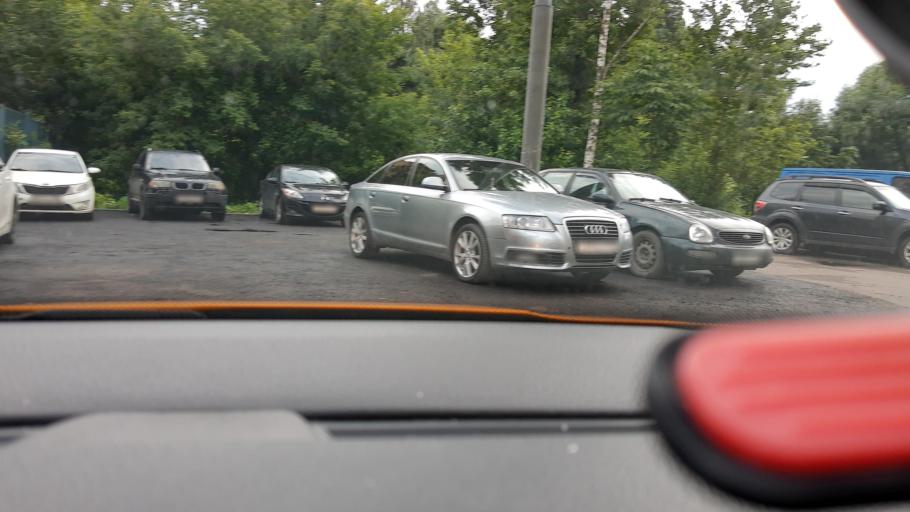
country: RU
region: Moskovskaya
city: Levoberezhnaya
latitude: 55.8972
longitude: 37.4781
